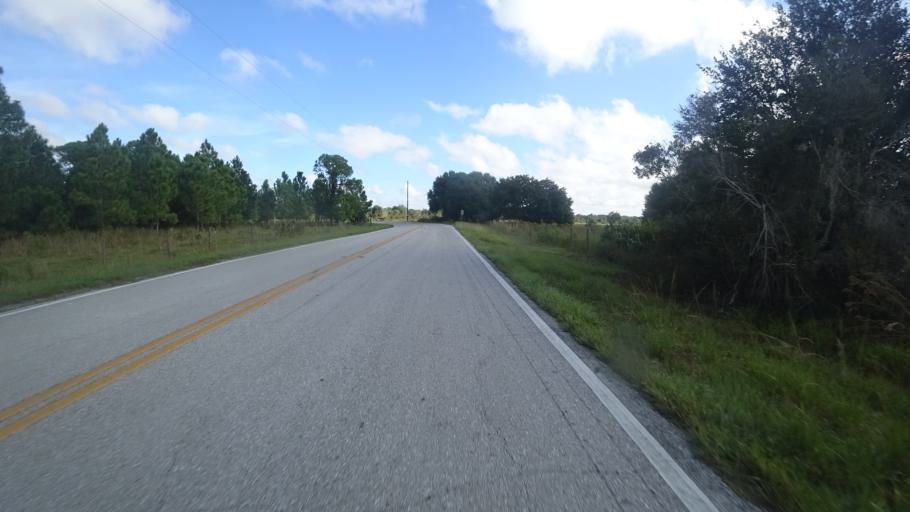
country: US
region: Florida
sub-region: Hardee County
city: Wauchula
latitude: 27.4940
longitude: -82.0712
